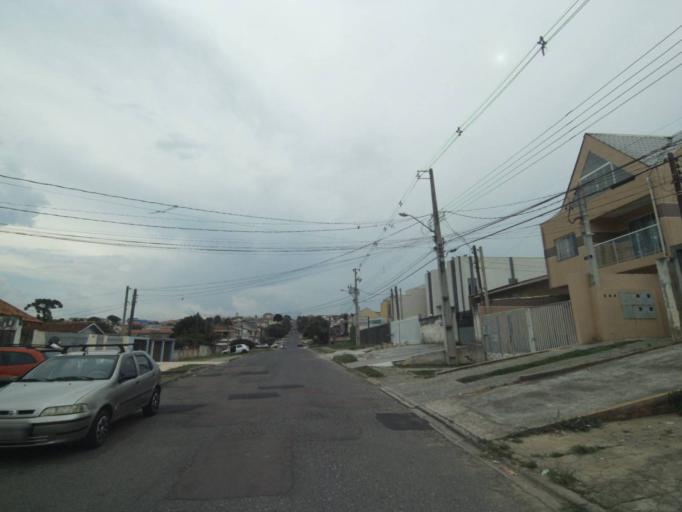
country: BR
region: Parana
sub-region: Pinhais
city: Pinhais
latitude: -25.3969
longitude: -49.2024
